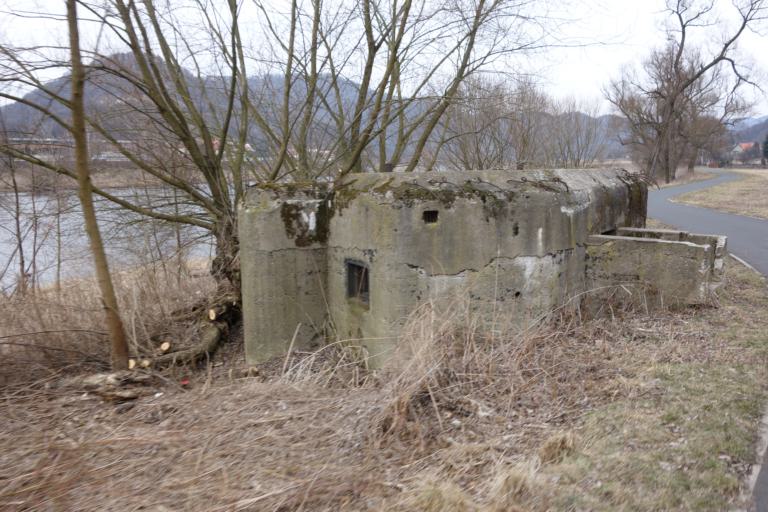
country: CZ
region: Ustecky
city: Povrly
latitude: 50.6686
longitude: 14.1630
